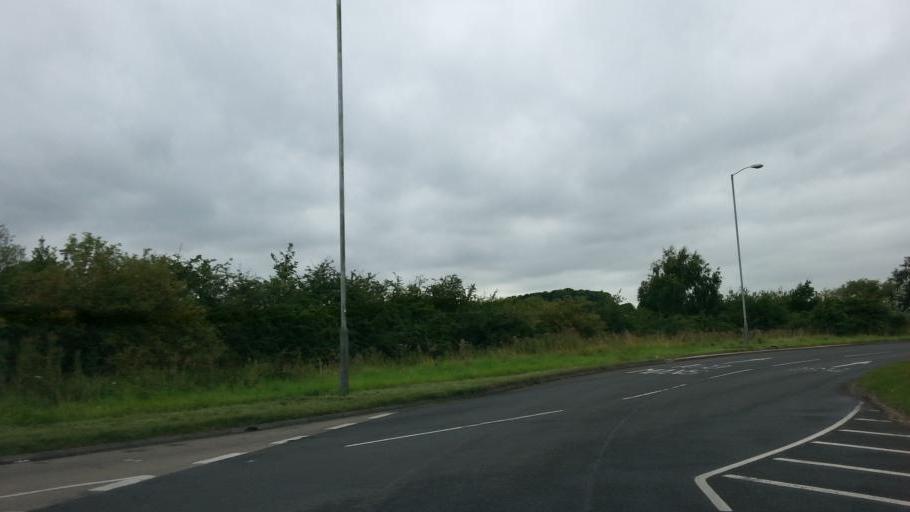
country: GB
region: England
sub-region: Nottinghamshire
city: Arnold
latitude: 53.0221
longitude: -1.1315
